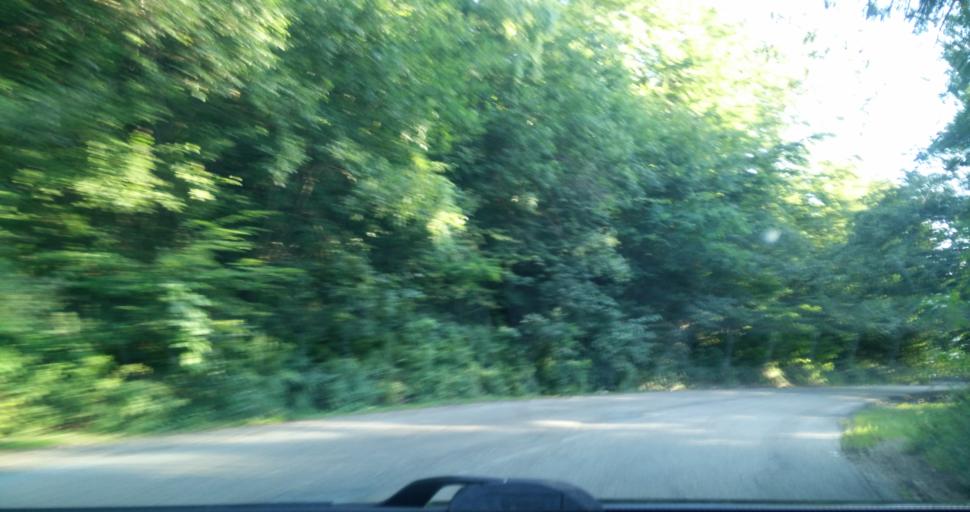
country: RO
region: Bihor
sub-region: Oras Nucet
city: Nucet
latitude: 46.4982
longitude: 22.6071
